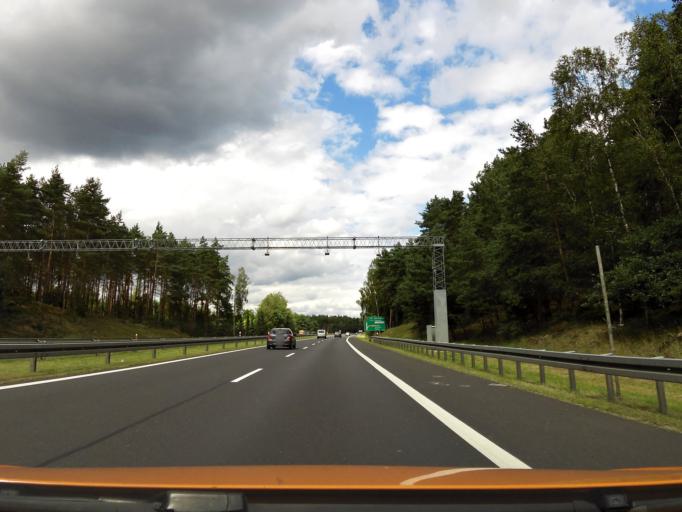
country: PL
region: West Pomeranian Voivodeship
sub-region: Powiat goleniowski
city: Goleniow
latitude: 53.5618
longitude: 14.7959
